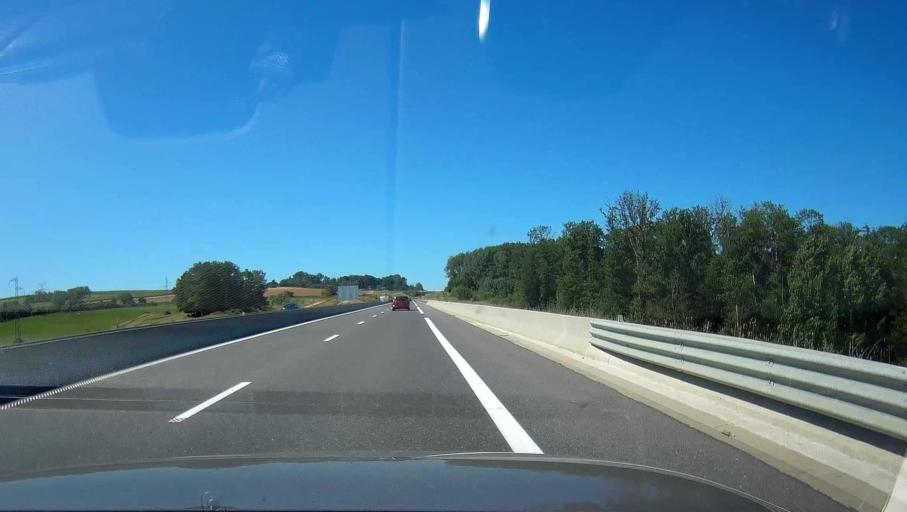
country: FR
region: Champagne-Ardenne
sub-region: Departement des Ardennes
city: Prix-les-Mezieres
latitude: 49.7354
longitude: 4.6863
